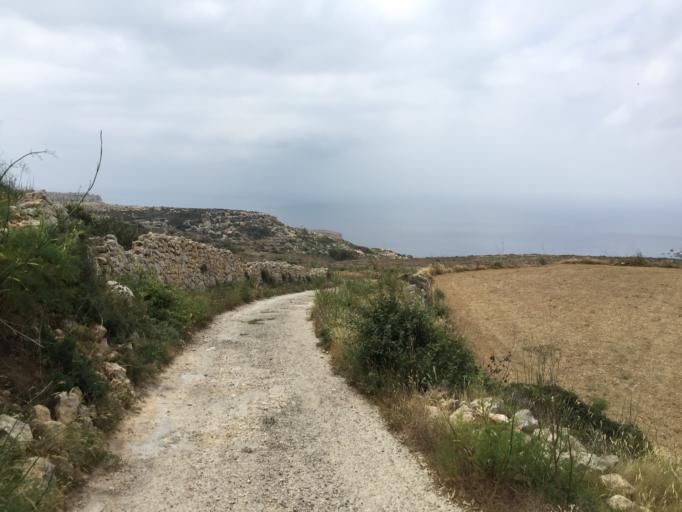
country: MT
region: L-Imgarr
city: Imgarr
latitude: 35.9018
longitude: 14.3467
